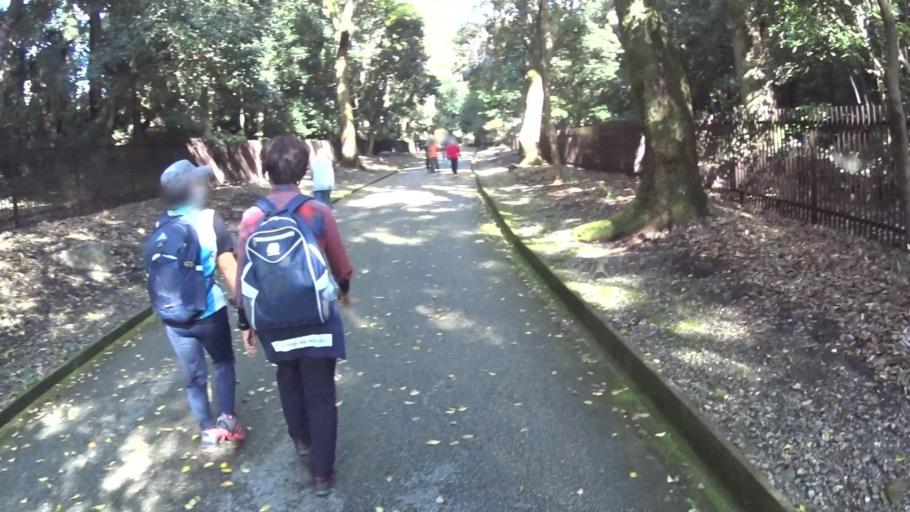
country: JP
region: Kyoto
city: Uji
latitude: 34.9363
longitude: 135.7751
